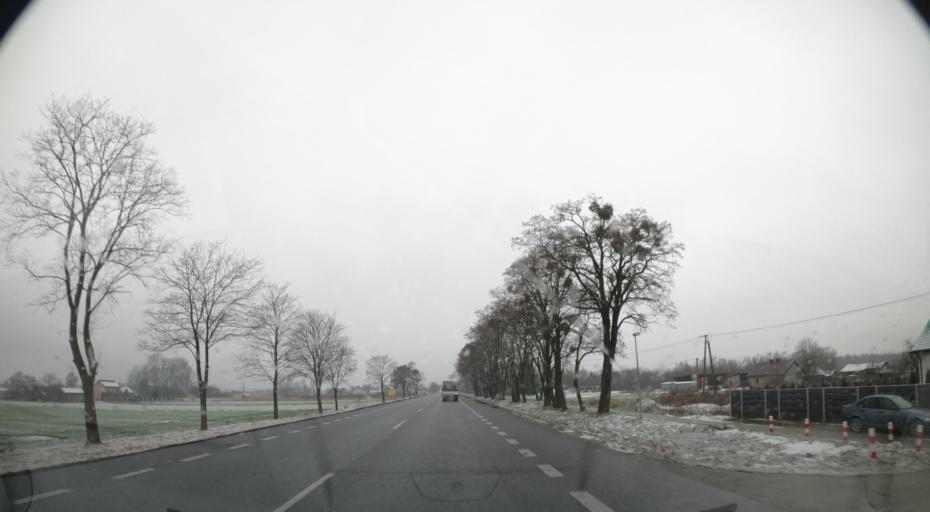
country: PL
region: Masovian Voivodeship
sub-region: Powiat sochaczewski
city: Teresin
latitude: 52.2142
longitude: 20.4048
